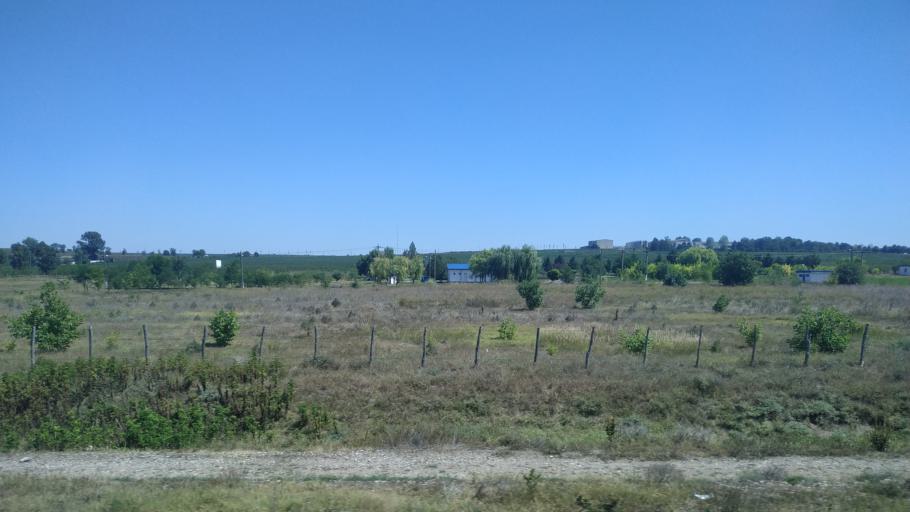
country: RO
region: Constanta
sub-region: Oras Murfatlar
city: Murfatlar
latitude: 44.1850
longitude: 28.3974
